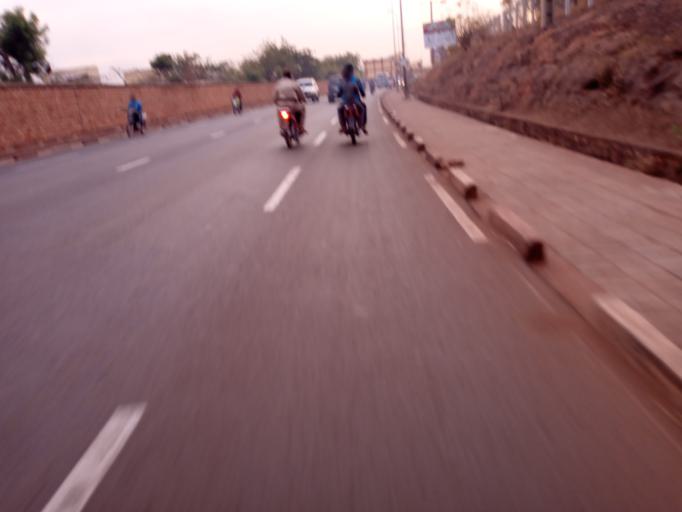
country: ML
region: Bamako
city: Bamako
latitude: 12.6563
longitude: -8.0026
